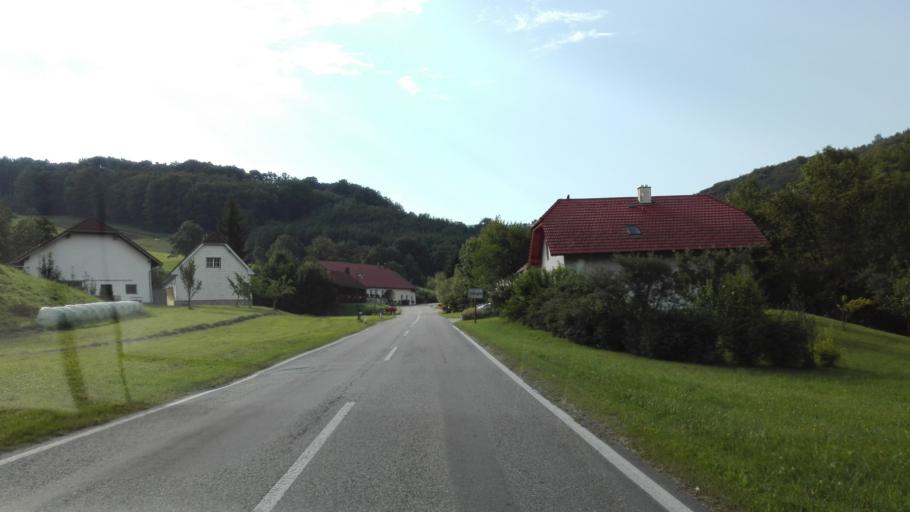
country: AT
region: Lower Austria
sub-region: Politischer Bezirk Sankt Polten
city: Stossing
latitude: 48.0991
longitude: 15.7676
